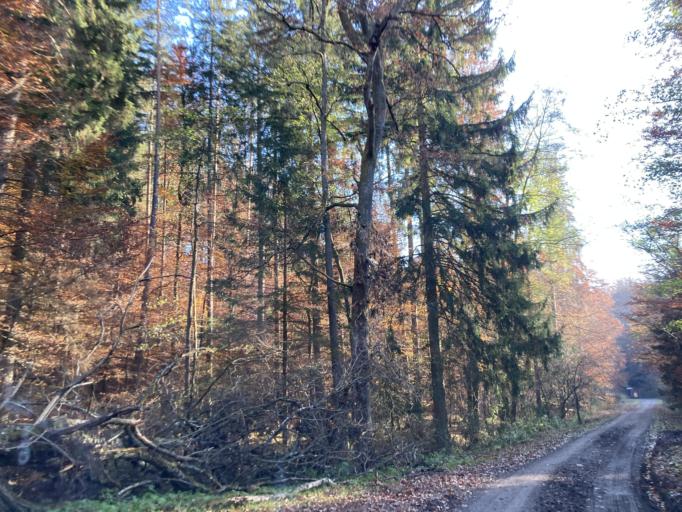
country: DE
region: Baden-Wuerttemberg
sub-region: Tuebingen Region
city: Tuebingen
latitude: 48.5451
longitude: 8.9931
